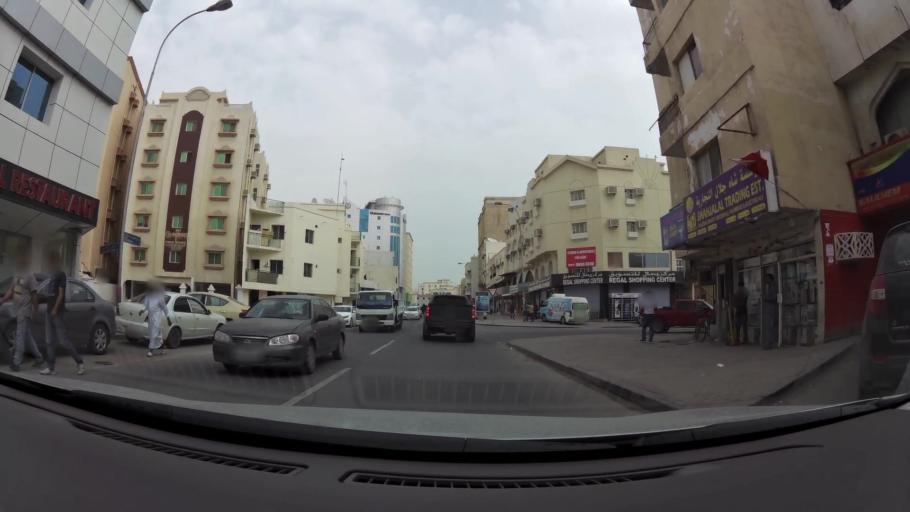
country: QA
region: Baladiyat ad Dawhah
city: Doha
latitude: 25.2671
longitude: 51.5381
